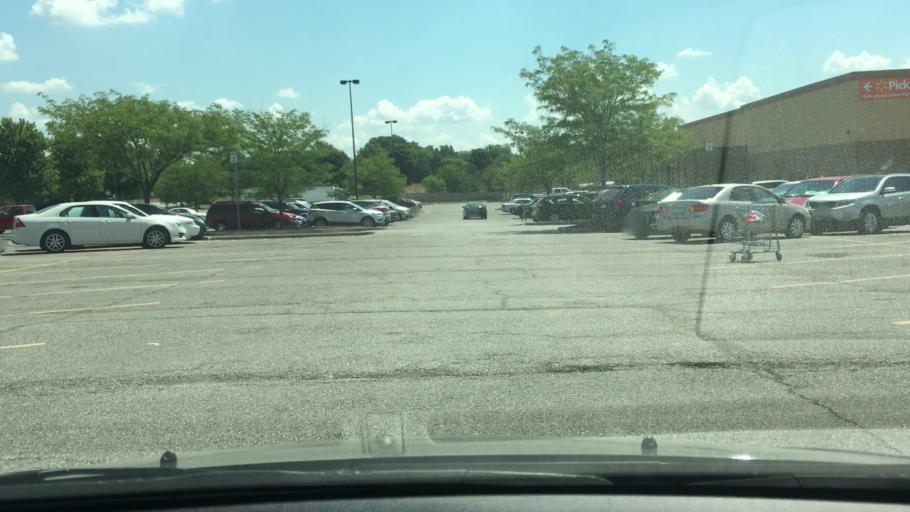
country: US
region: Missouri
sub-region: Jackson County
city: Grandview
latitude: 38.8860
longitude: -94.6062
